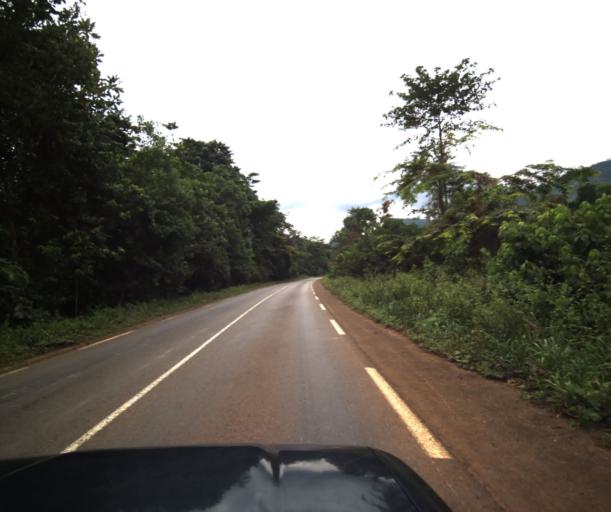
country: CM
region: Centre
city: Eseka
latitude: 3.8903
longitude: 10.7853
